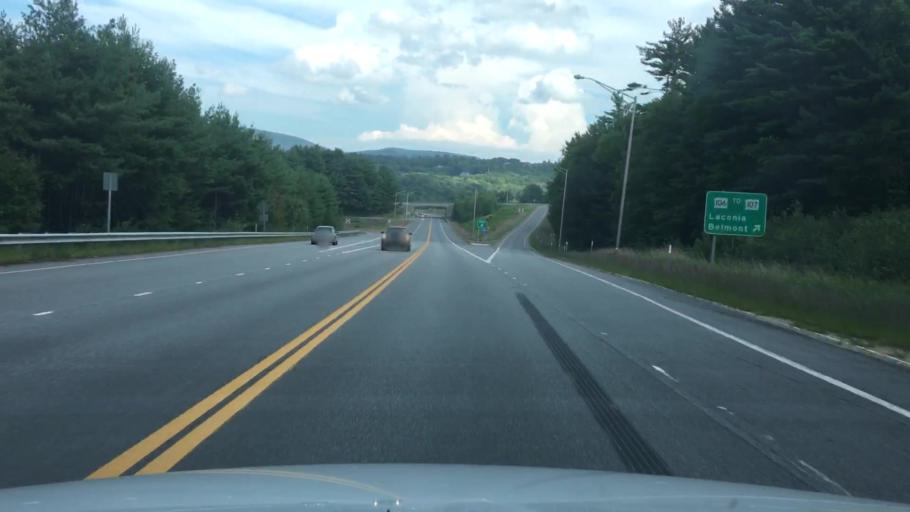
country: US
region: New Hampshire
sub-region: Belknap County
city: Laconia
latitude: 43.5128
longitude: -71.4647
